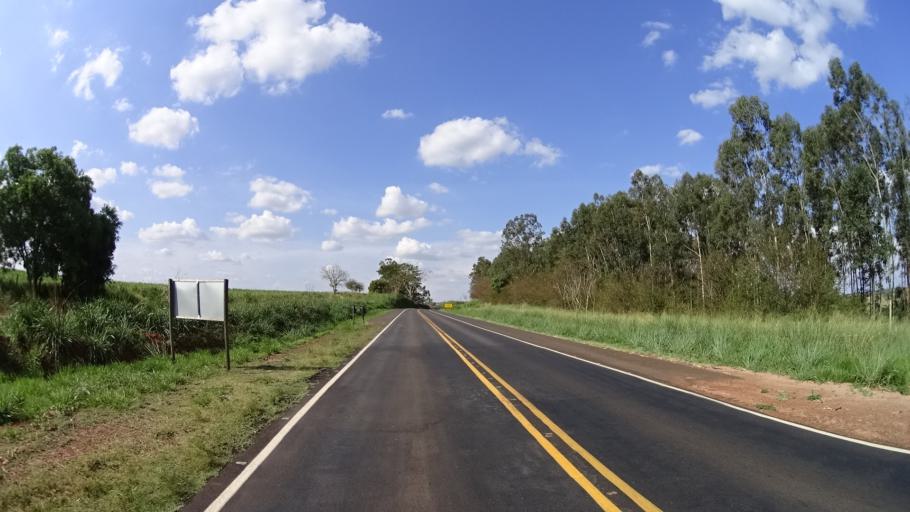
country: BR
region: Sao Paulo
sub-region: Urupes
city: Urupes
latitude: -21.0129
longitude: -49.2273
